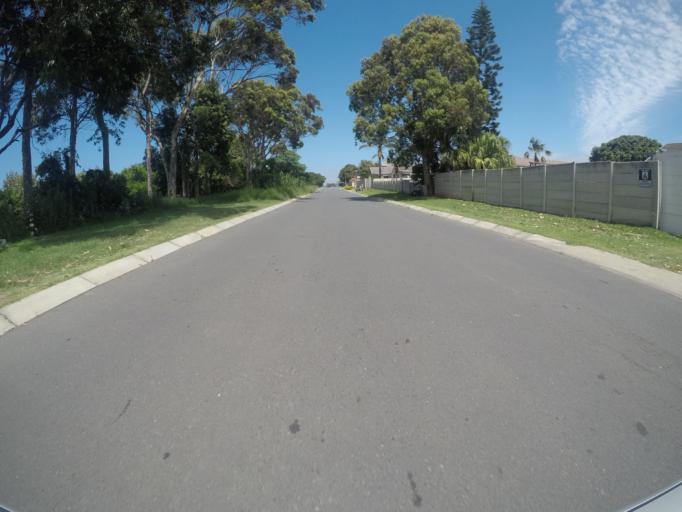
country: ZA
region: Eastern Cape
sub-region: Buffalo City Metropolitan Municipality
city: East London
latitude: -32.9496
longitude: 28.0009
